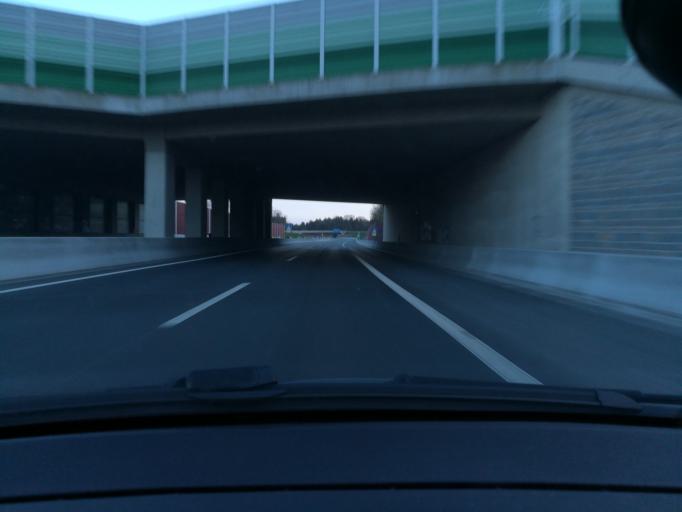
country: DE
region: North Rhine-Westphalia
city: Halle
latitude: 52.0490
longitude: 8.3402
